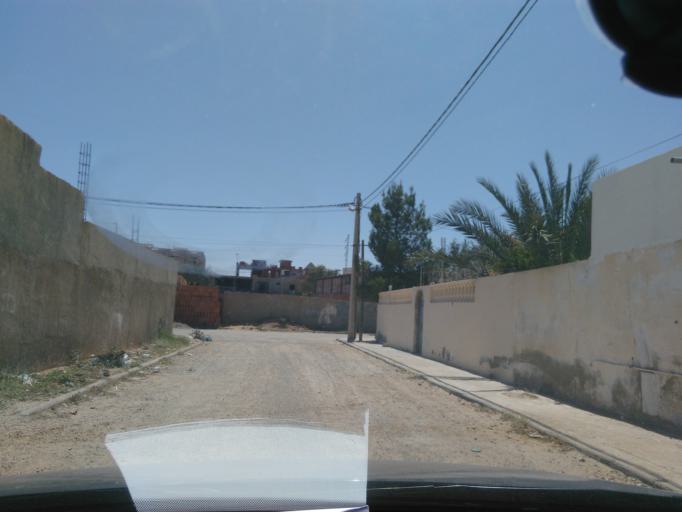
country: TN
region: Tataouine
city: Tataouine
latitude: 32.9479
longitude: 10.4637
